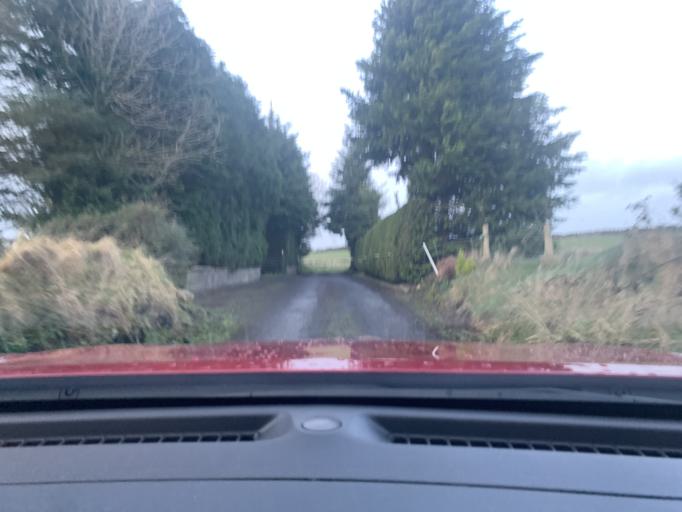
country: IE
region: Connaught
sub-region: Sligo
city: Ballymote
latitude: 53.9918
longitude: -8.4378
